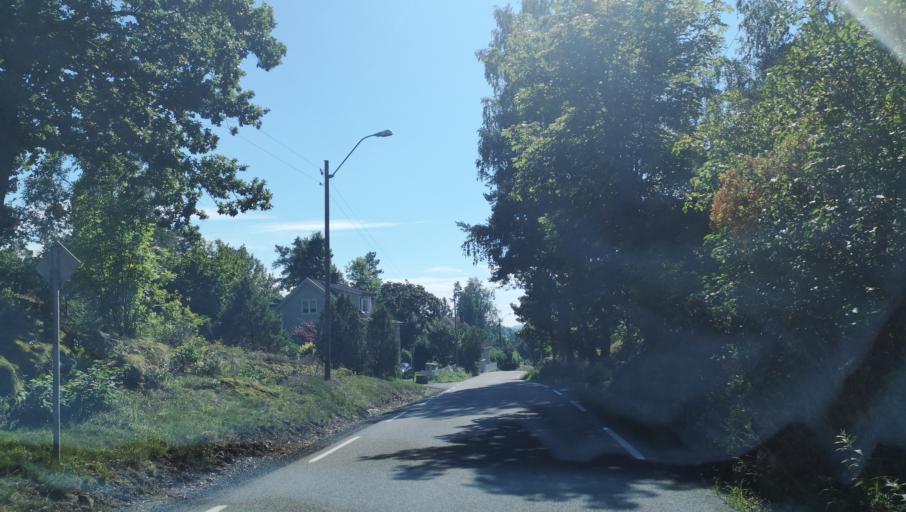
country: NO
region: Akershus
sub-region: Vestby
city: Vestby
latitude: 59.5363
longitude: 10.6901
